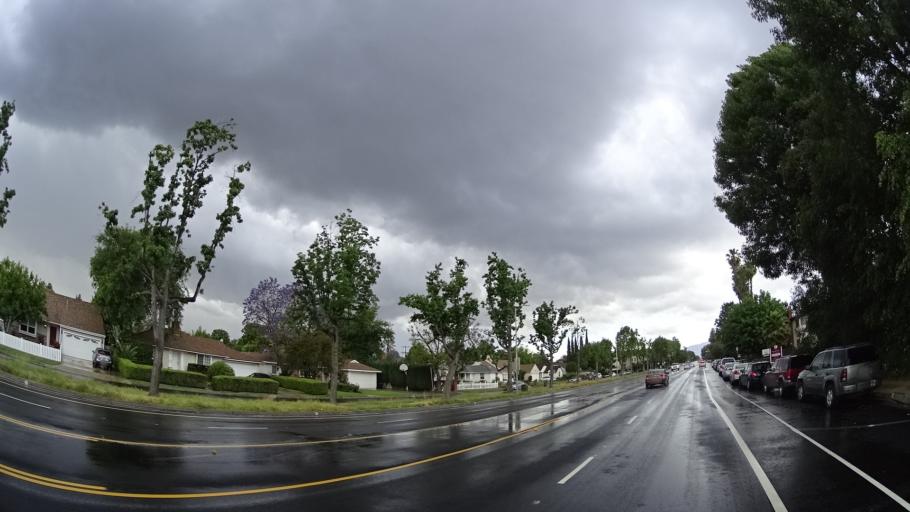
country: US
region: California
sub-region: Los Angeles County
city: Sherman Oaks
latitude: 34.1595
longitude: -118.4311
